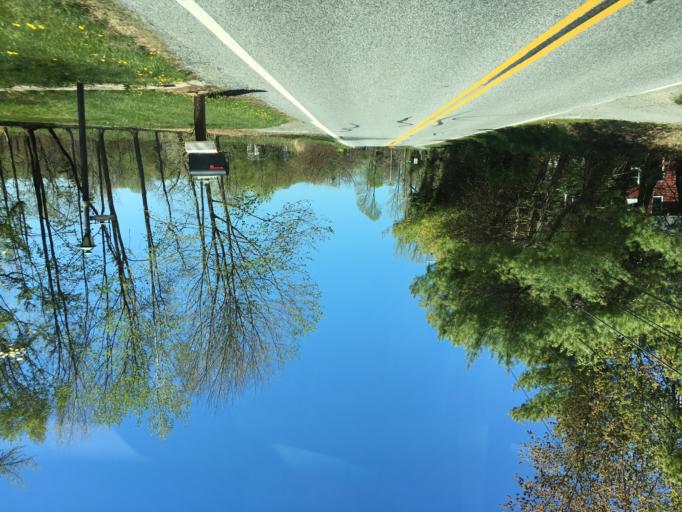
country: US
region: Maryland
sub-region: Baltimore County
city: Hunt Valley
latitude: 39.5916
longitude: -76.6427
